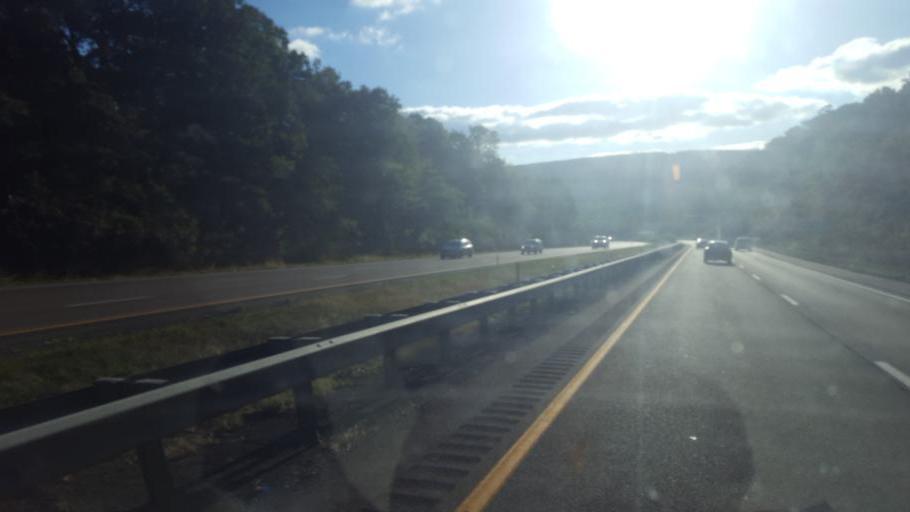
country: US
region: Maryland
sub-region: Allegany County
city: La Vale
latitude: 39.6357
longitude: -78.8481
